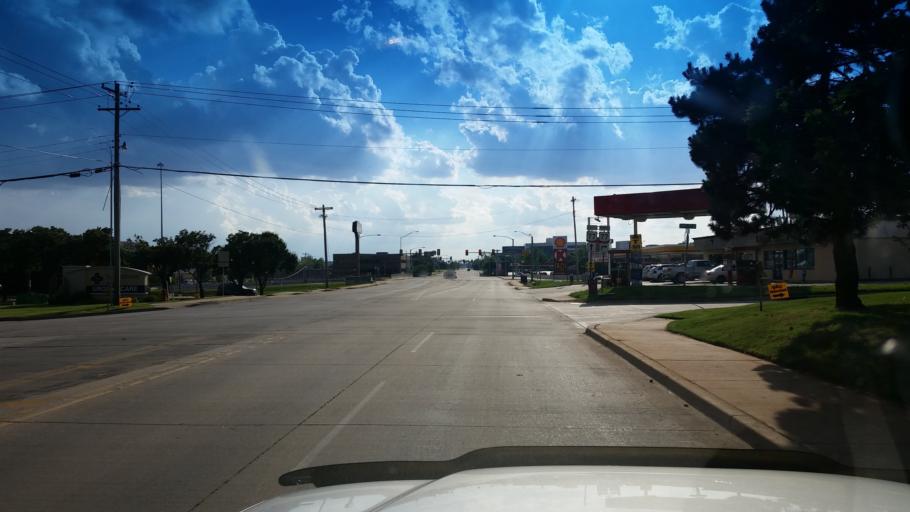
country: US
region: Oklahoma
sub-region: Oklahoma County
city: Nichols Hills
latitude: 35.5369
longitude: -97.5117
